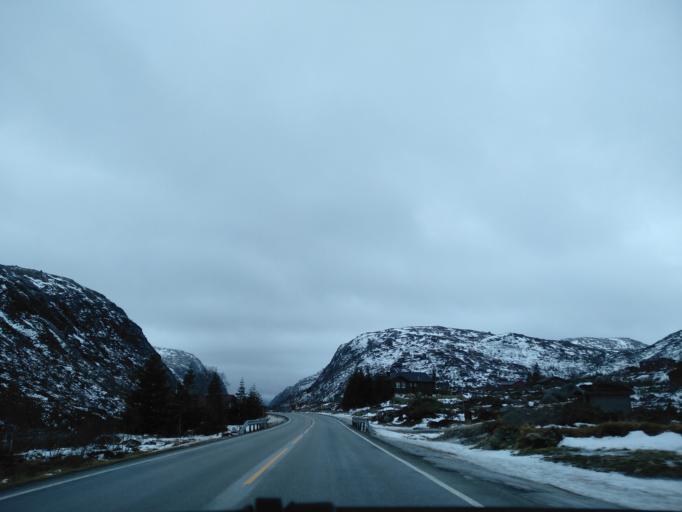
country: NO
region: Vest-Agder
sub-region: Sirdal
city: Tonstad
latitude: 58.8762
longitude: 6.5947
